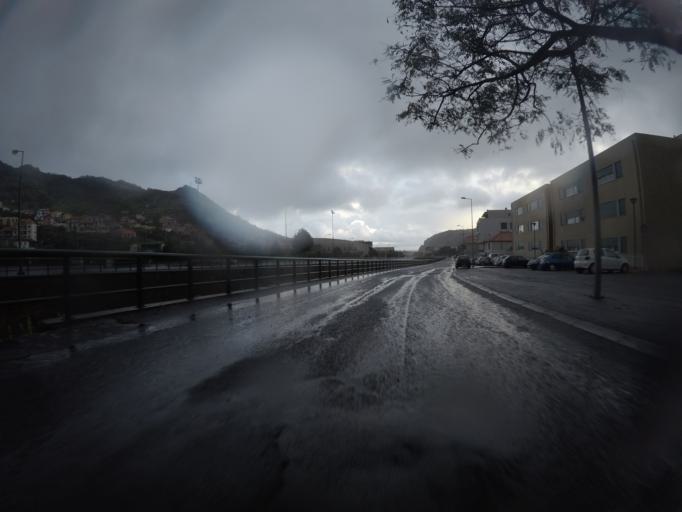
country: PT
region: Madeira
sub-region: Machico
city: Machico
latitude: 32.7276
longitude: -16.7731
